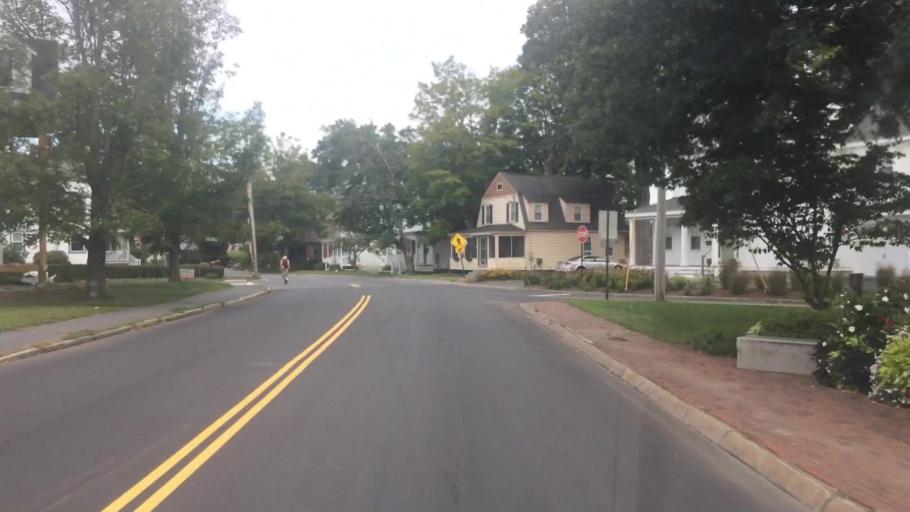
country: US
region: Massachusetts
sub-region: Middlesex County
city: West Concord
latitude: 42.4583
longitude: -71.3974
